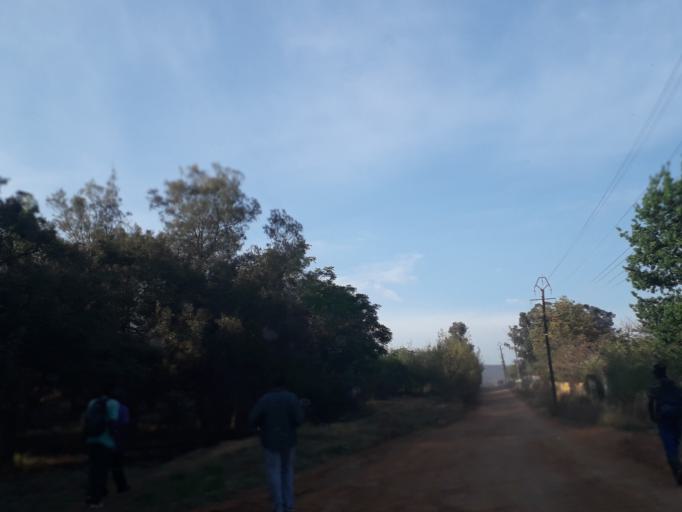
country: ZA
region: Gauteng
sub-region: City of Johannesburg Metropolitan Municipality
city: Roodepoort
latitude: -26.0981
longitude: 27.8955
